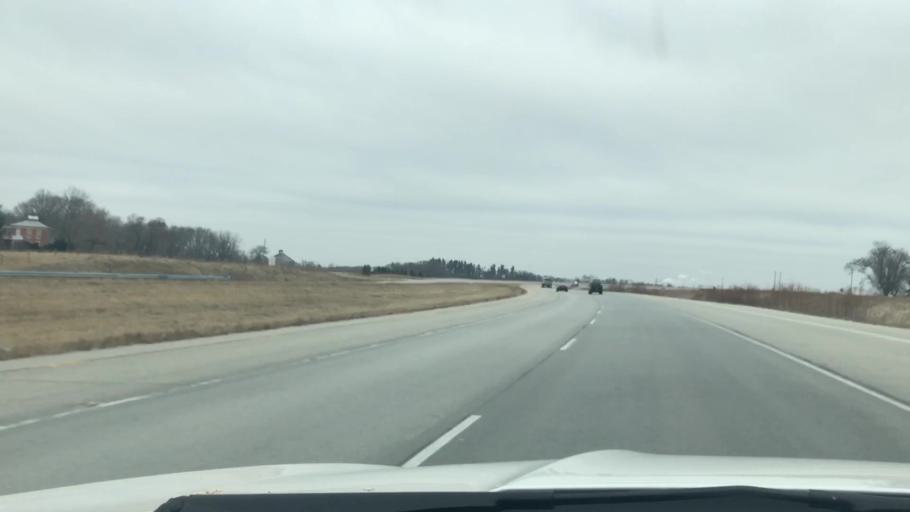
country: US
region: Indiana
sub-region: Cass County
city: Georgetown
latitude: 40.7044
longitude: -86.4568
